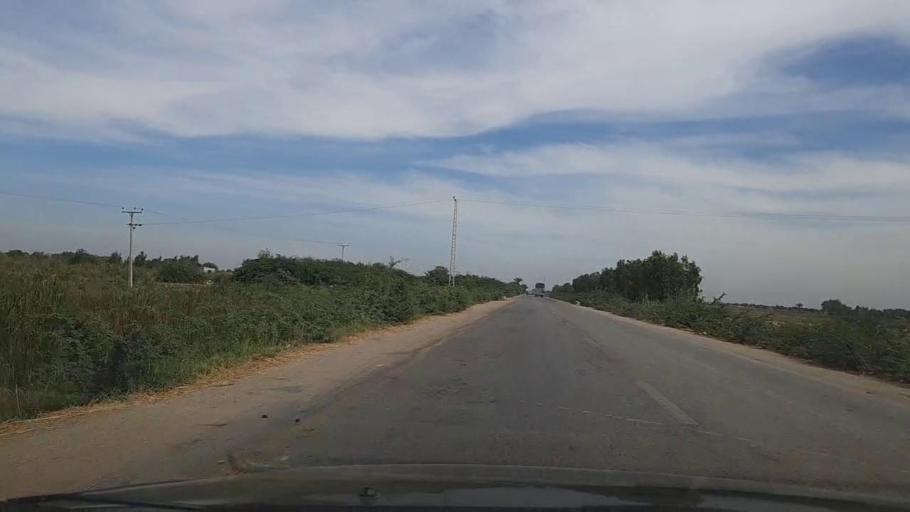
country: PK
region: Sindh
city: Thatta
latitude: 24.7994
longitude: 67.9642
